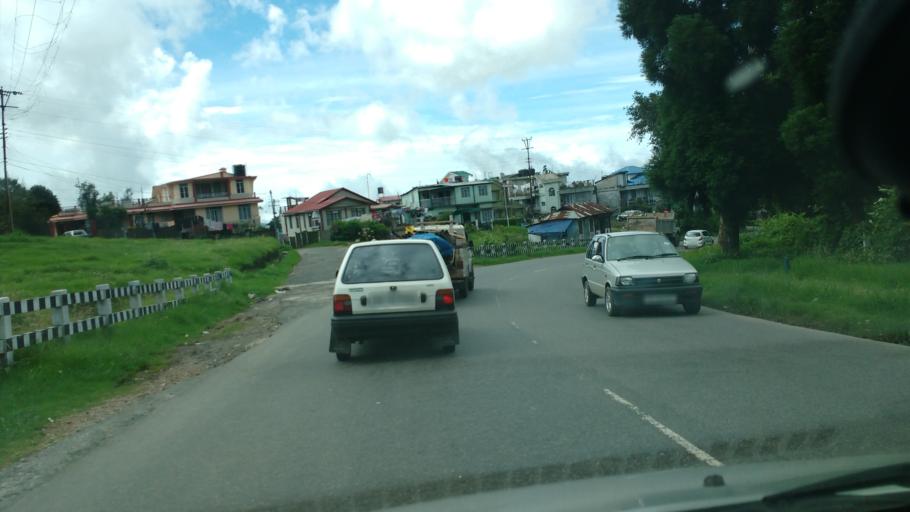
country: IN
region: Meghalaya
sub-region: East Khasi Hills
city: Shillong
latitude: 25.5492
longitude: 91.8417
